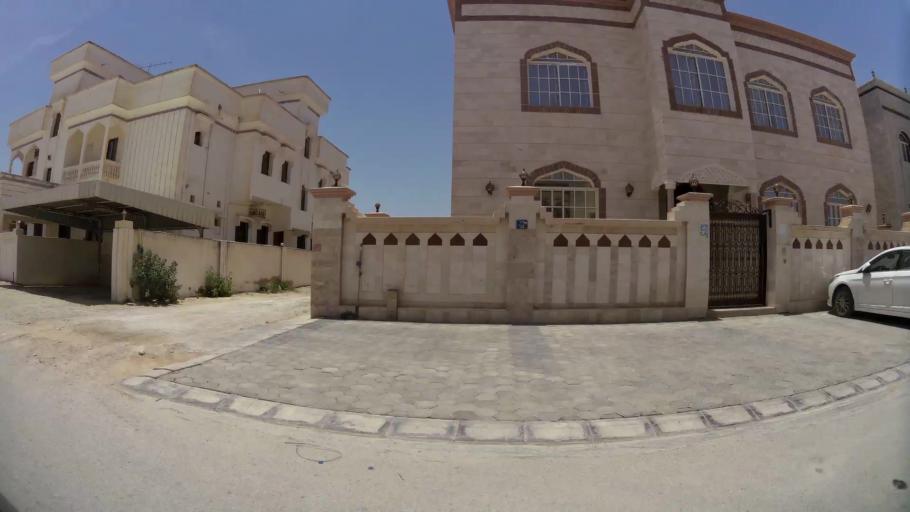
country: OM
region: Zufar
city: Salalah
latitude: 17.0789
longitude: 54.1577
